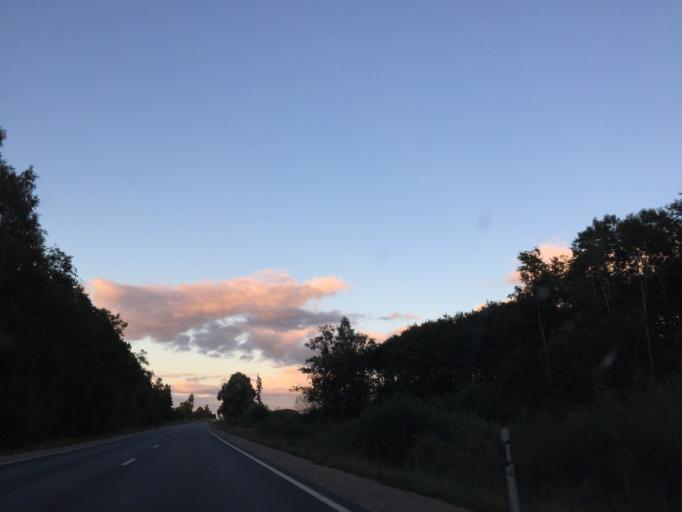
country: LV
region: Jaunpils
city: Jaunpils
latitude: 56.6979
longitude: 23.1485
